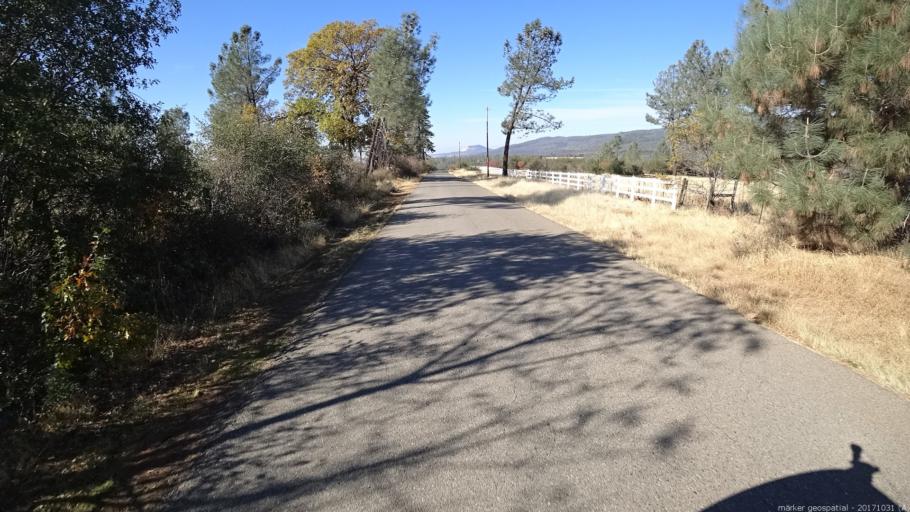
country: US
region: California
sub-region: Shasta County
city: Shingletown
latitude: 40.4463
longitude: -121.8571
